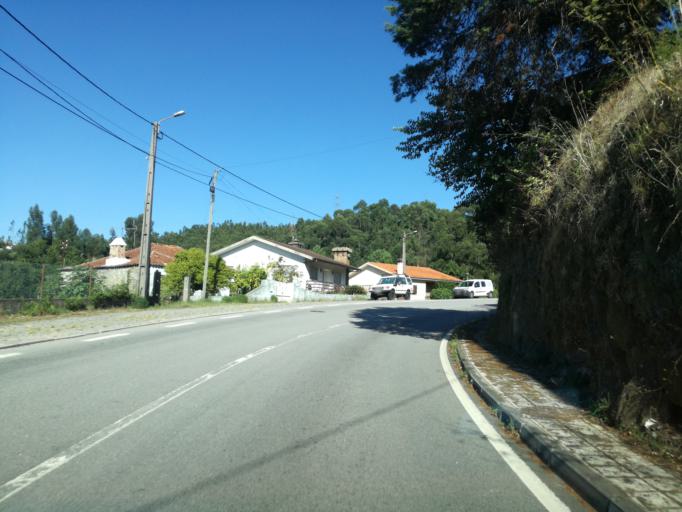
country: PT
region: Porto
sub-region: Pacos de Ferreira
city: Seroa
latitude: 41.2585
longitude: -8.4663
